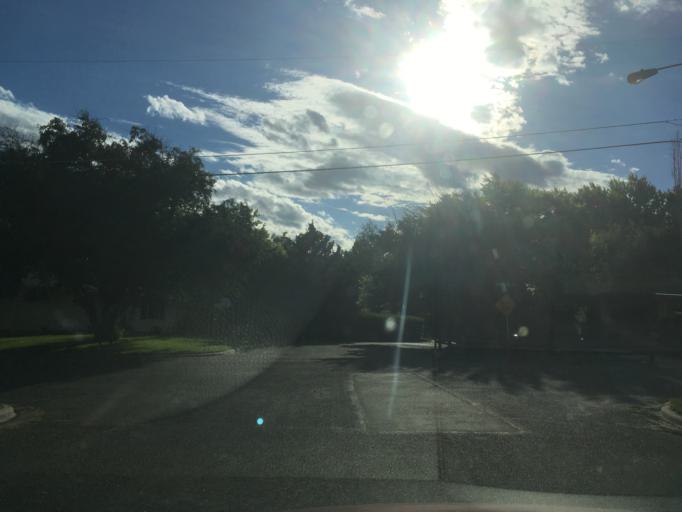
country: US
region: Montana
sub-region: Yellowstone County
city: Billings
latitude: 45.7975
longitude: -108.5788
